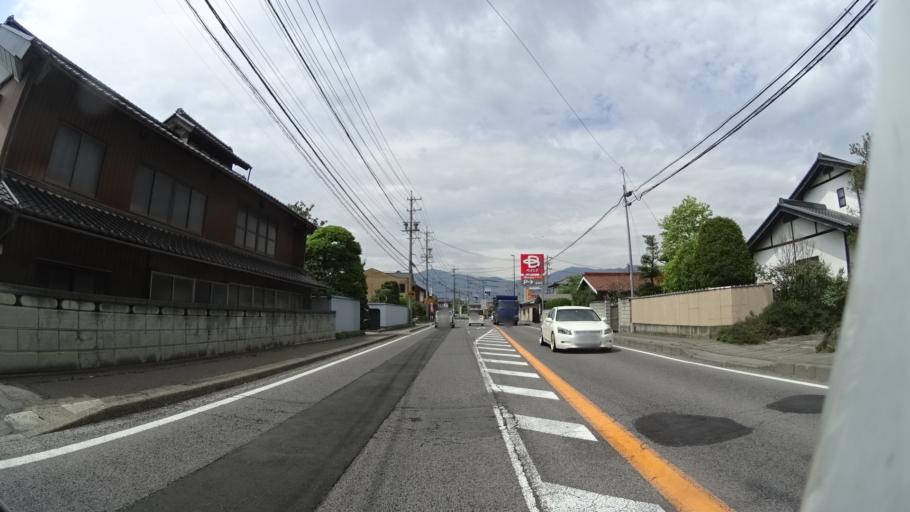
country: JP
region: Nagano
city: Ueda
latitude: 36.4273
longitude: 138.1930
